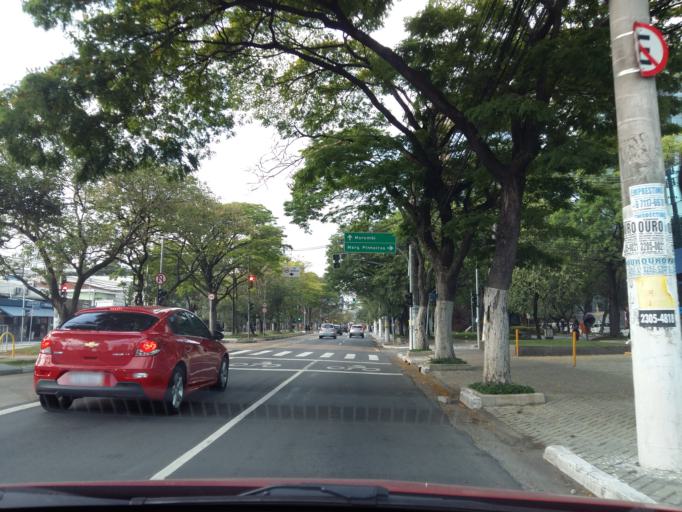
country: BR
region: Sao Paulo
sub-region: Sao Paulo
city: Sao Paulo
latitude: -23.6017
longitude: -46.6917
